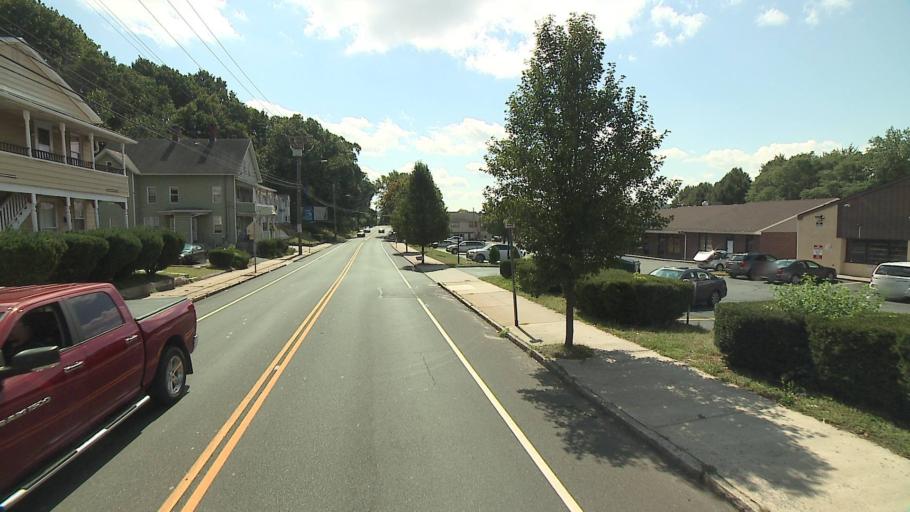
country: US
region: Connecticut
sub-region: New Haven County
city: Ansonia
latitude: 41.3522
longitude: -73.0810
